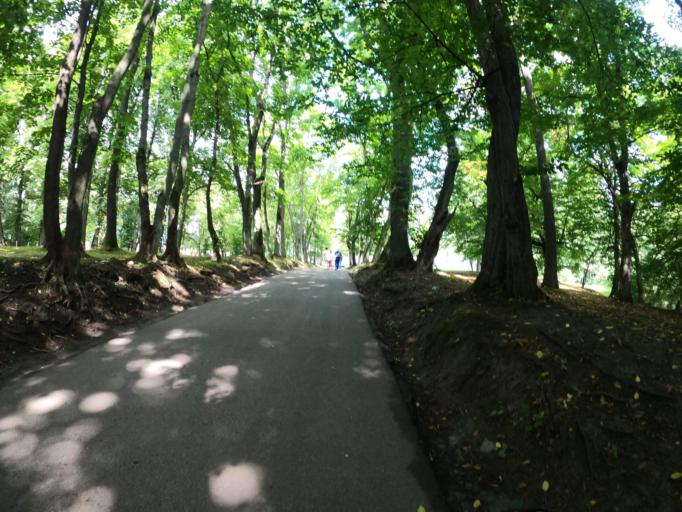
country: RU
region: Kaliningrad
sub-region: Gorod Kaliningrad
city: Kaliningrad
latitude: 54.7163
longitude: 20.4762
